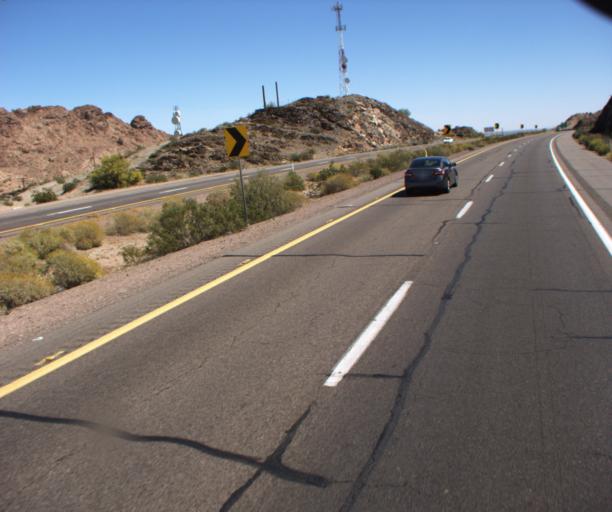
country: US
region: Arizona
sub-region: Yuma County
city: Wellton
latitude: 32.7257
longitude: -113.7494
